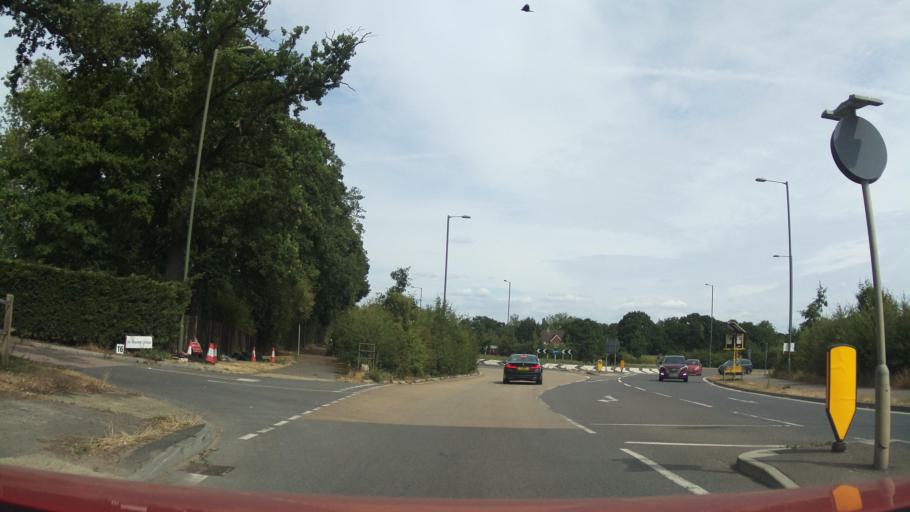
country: GB
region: England
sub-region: Surrey
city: Salfords
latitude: 51.1885
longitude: -0.1962
